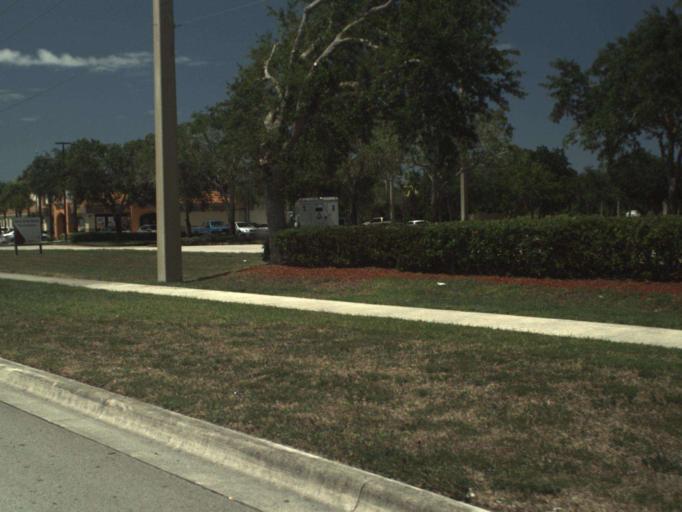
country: US
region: Florida
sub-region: Saint Lucie County
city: River Park
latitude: 27.3004
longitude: -80.3053
